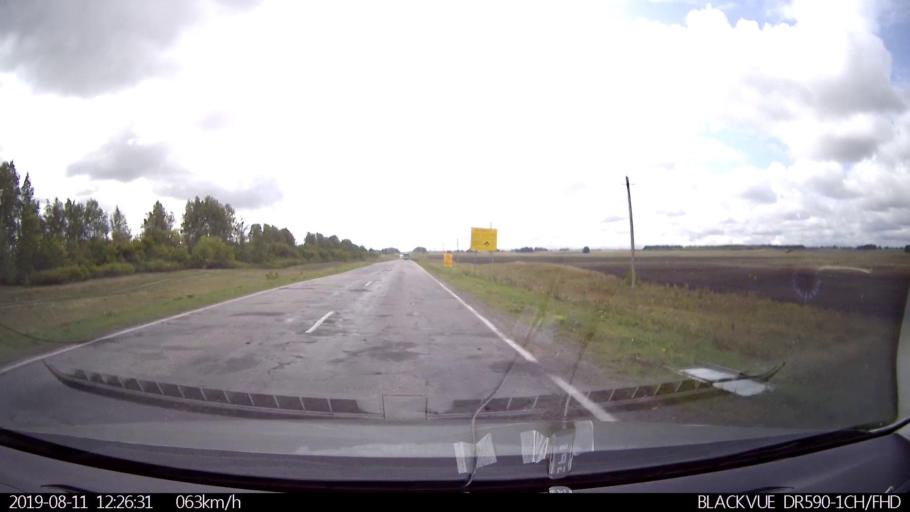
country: RU
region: Ulyanovsk
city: Ignatovka
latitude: 53.8633
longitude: 47.9298
